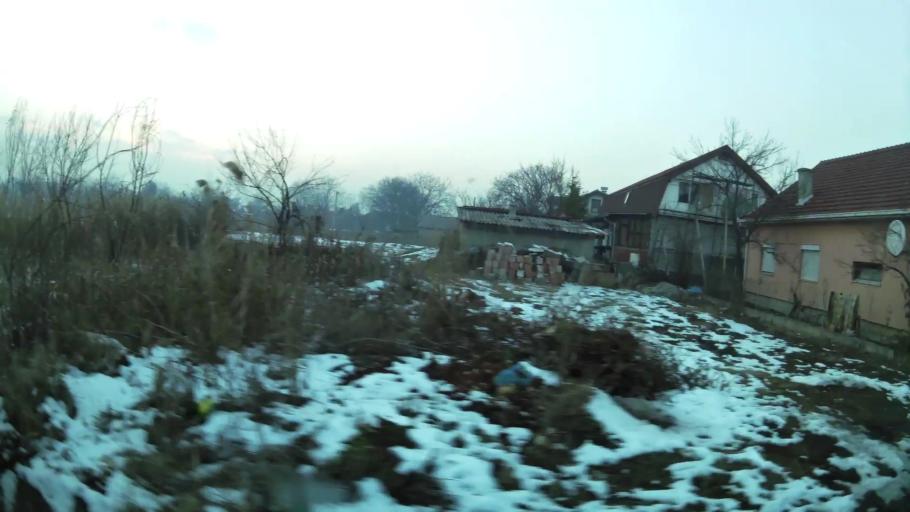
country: MK
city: Creshevo
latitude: 42.0007
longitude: 21.5095
